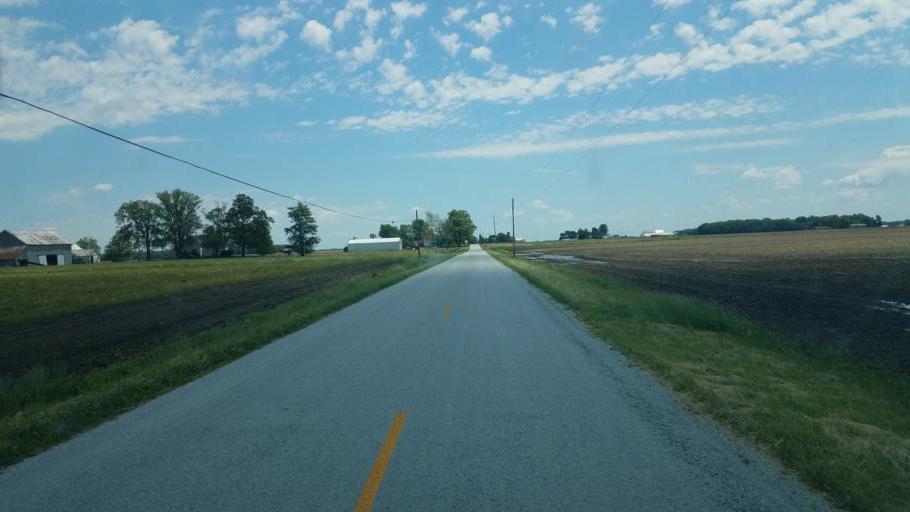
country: US
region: Ohio
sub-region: Hardin County
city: Forest
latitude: 40.6870
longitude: -83.4728
